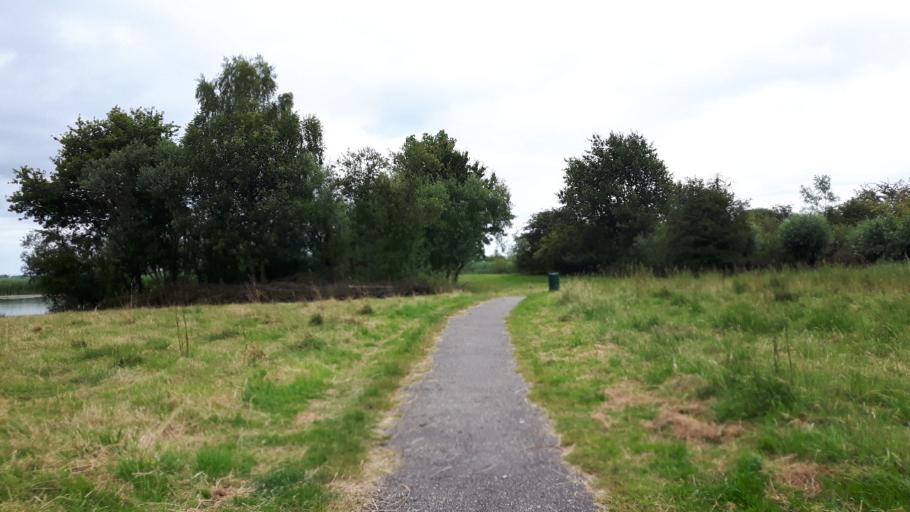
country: NL
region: South Holland
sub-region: Gemeente Schiedam
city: Schiedam
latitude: 51.9500
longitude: 4.4197
